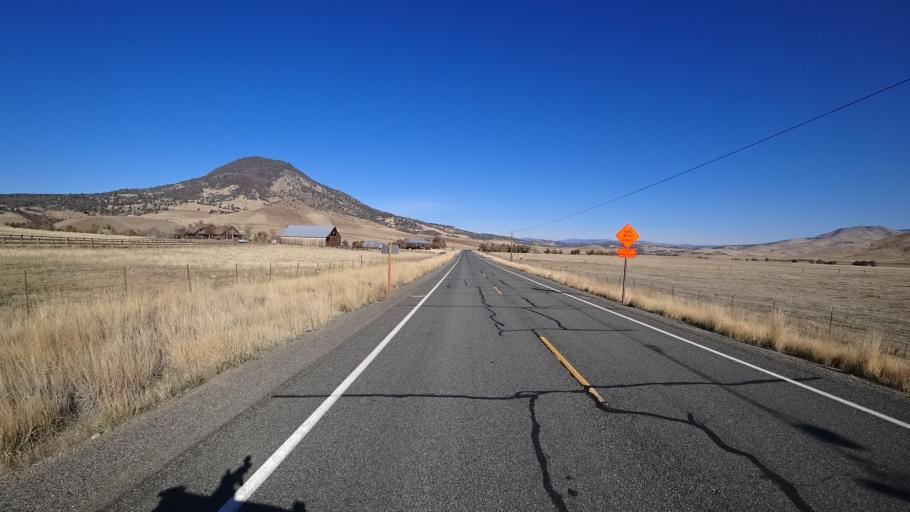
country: US
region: California
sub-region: Siskiyou County
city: Montague
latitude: 41.8240
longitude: -122.4947
